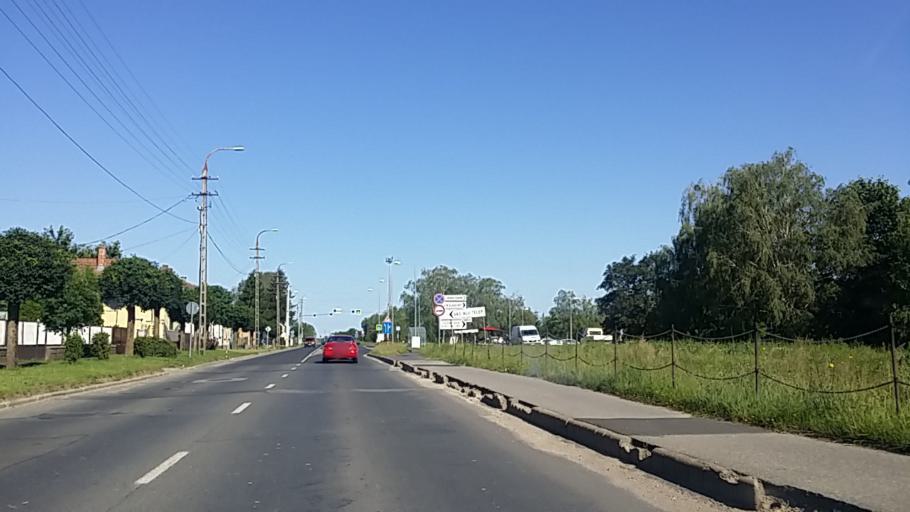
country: HU
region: Zala
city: Zalaegerszeg
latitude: 46.8523
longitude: 16.8143
